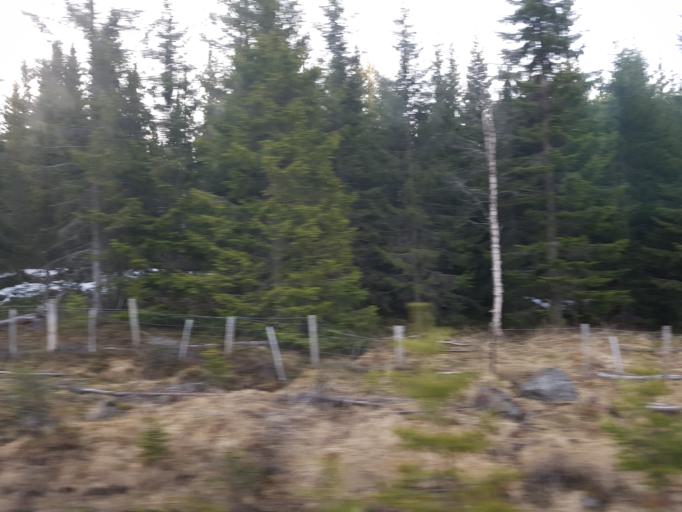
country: NO
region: Sor-Trondelag
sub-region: Rennebu
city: Berkak
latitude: 62.8649
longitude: 10.0270
